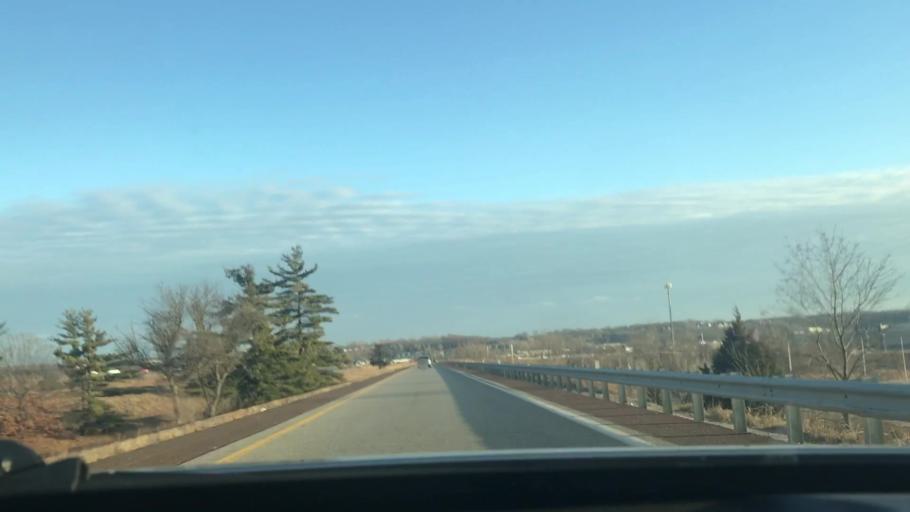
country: US
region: Missouri
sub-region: Jackson County
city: East Independence
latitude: 39.0409
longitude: -94.3660
